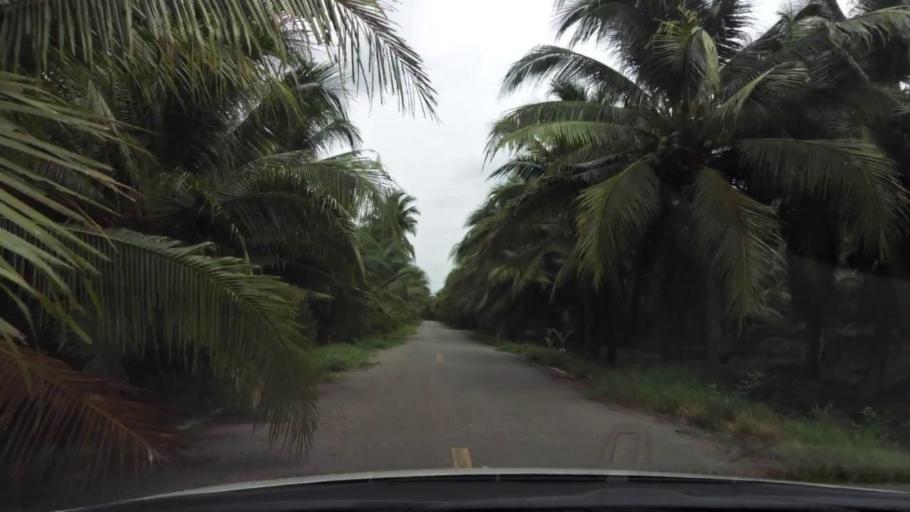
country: TH
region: Samut Sakhon
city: Ban Phaeo
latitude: 13.6055
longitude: 100.0331
